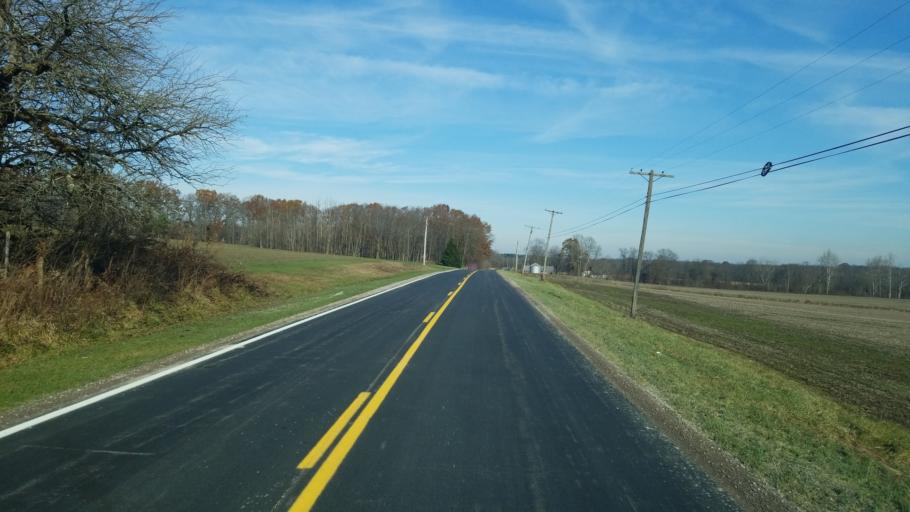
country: US
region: Ohio
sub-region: Ashtabula County
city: Roaming Shores
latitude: 41.6813
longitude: -80.9089
